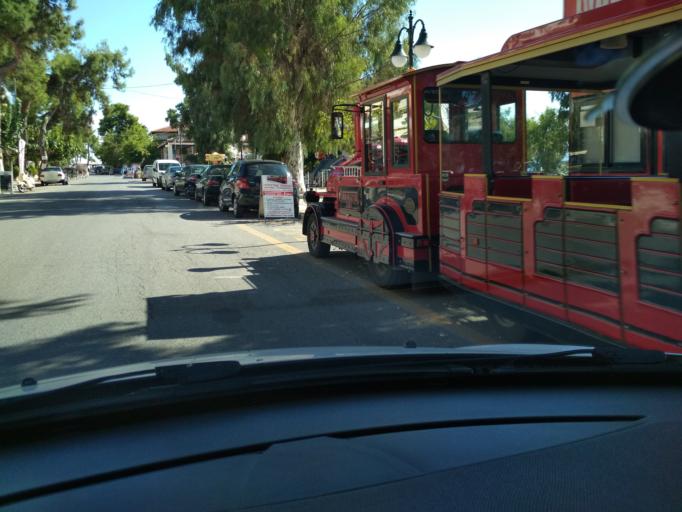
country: GR
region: Central Greece
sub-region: Nomos Evvoias
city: Oreoi
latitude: 38.8569
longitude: 23.0418
